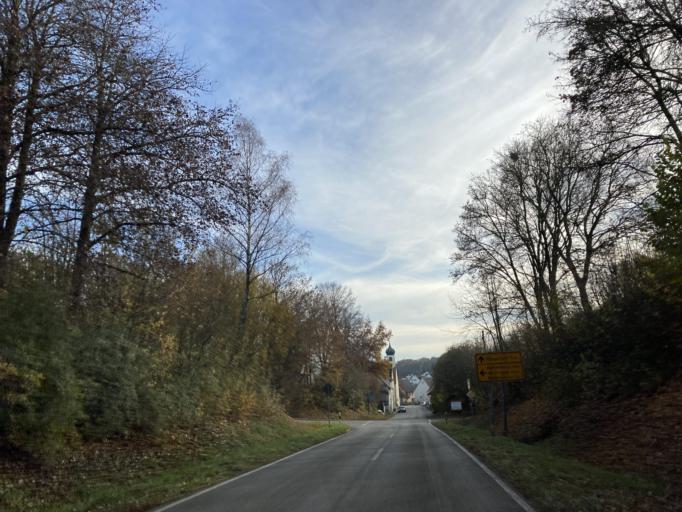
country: DE
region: Baden-Wuerttemberg
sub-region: Tuebingen Region
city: Hirrlingen
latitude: 48.4041
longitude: 8.8537
